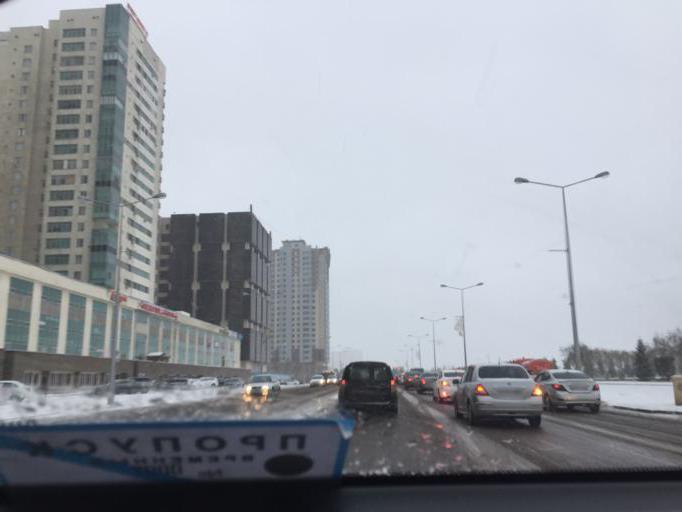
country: KZ
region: Astana Qalasy
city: Astana
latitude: 51.1321
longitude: 71.4592
